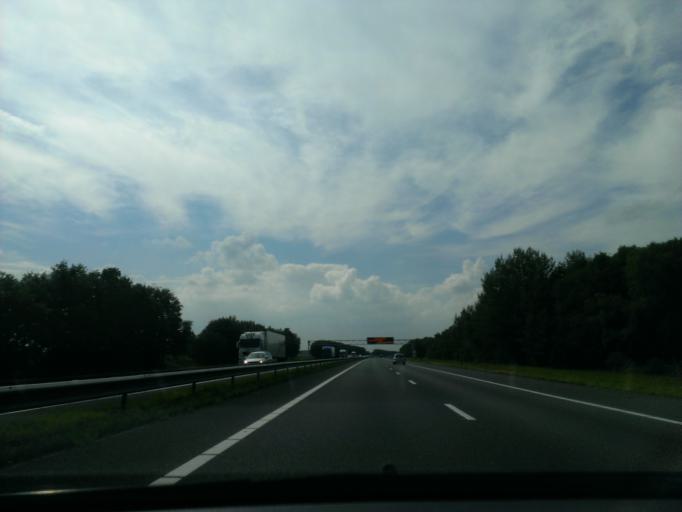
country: NL
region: Gelderland
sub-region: Gemeente Barneveld
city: Voorthuizen
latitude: 52.1714
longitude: 5.6273
